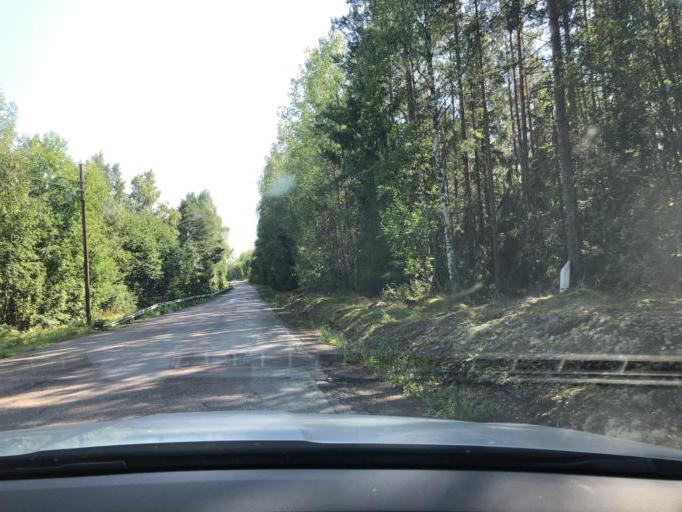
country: SE
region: Dalarna
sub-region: Hedemora Kommun
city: Hedemora
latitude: 60.3250
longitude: 15.9143
